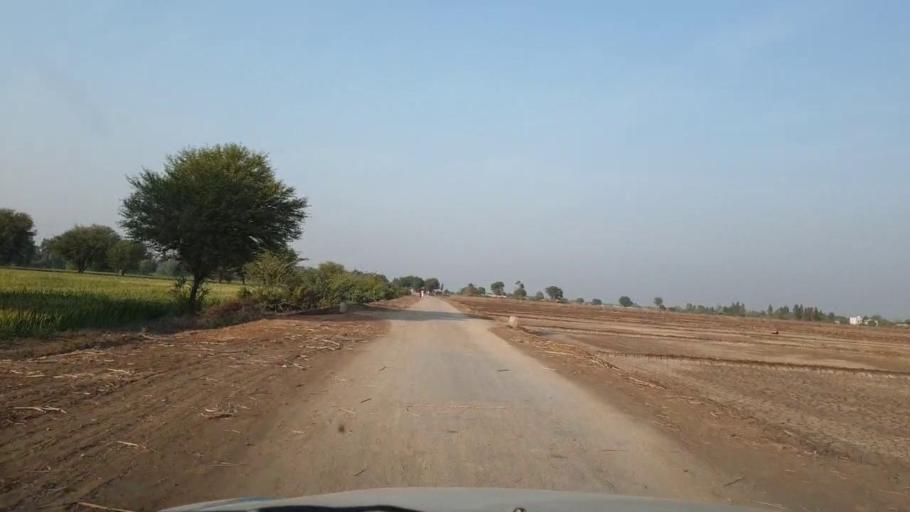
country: PK
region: Sindh
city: Pithoro
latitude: 25.6743
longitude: 69.2041
